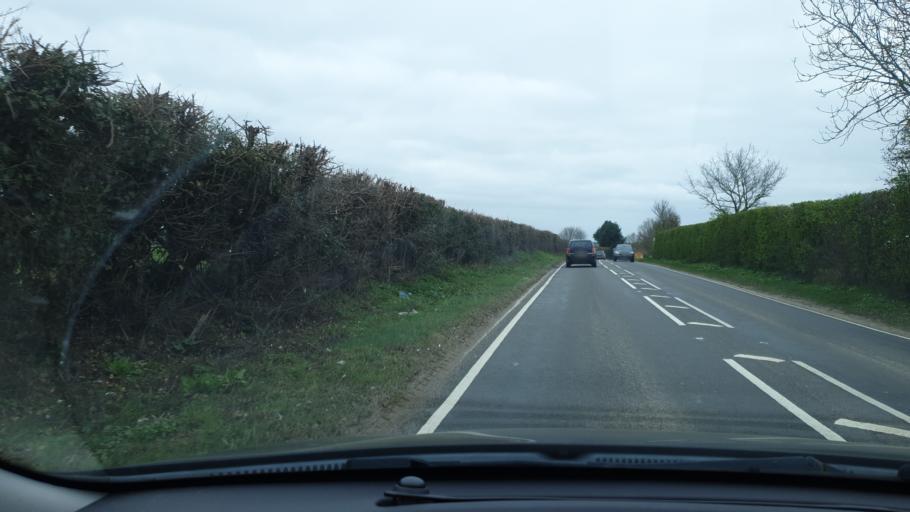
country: GB
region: England
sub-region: Essex
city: Great Horkesley
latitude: 51.9575
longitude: 0.8705
